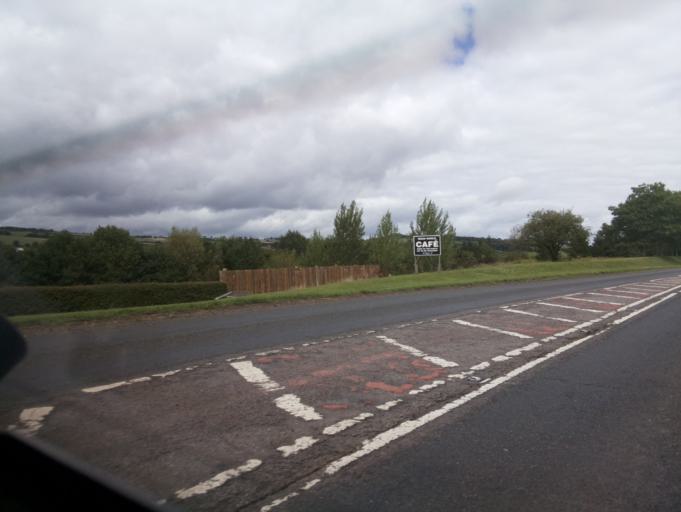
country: GB
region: England
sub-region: Devon
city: Bradninch
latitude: 50.8143
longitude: -3.4176
